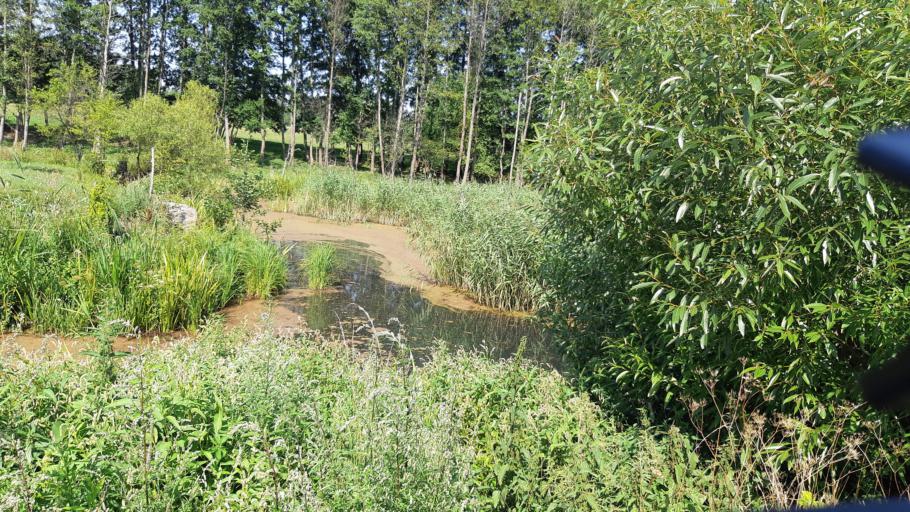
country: LT
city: Virbalis
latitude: 54.6446
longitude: 22.8178
